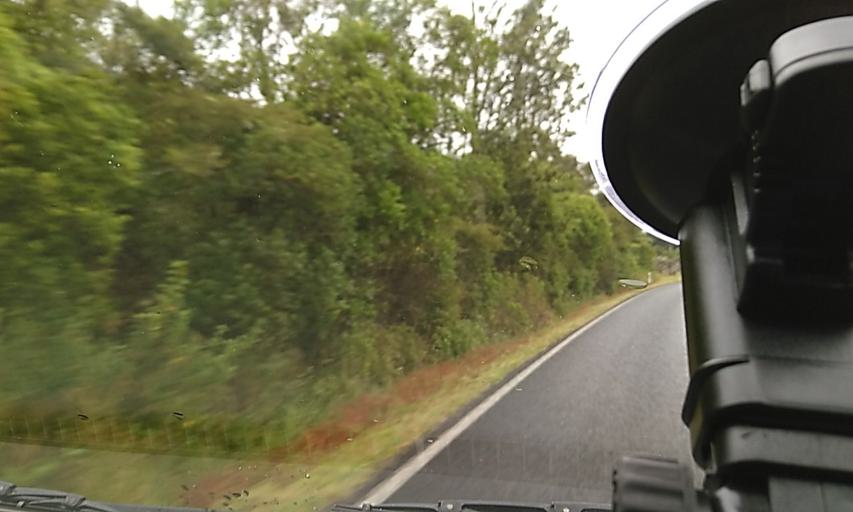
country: NZ
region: Auckland
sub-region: Auckland
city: Pukekohe East
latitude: -37.3164
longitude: 174.9371
